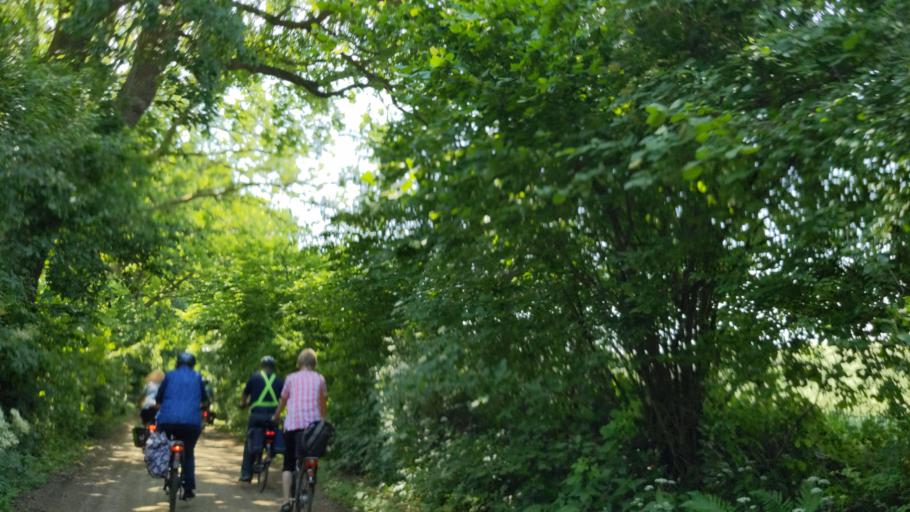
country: DE
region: Schleswig-Holstein
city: Albsfelde
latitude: 53.6797
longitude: 10.7011
